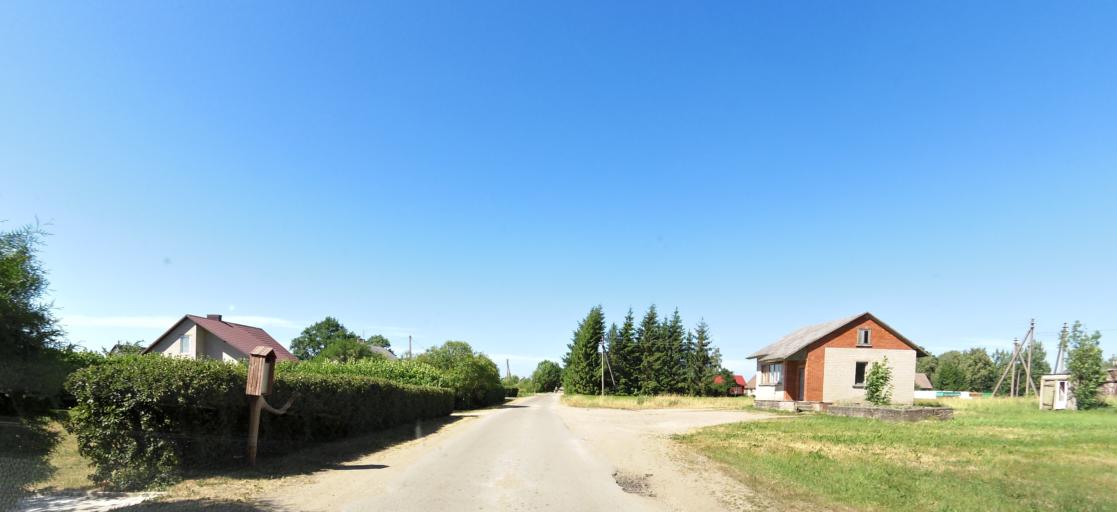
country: LT
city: Vabalninkas
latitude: 55.9728
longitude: 24.6616
